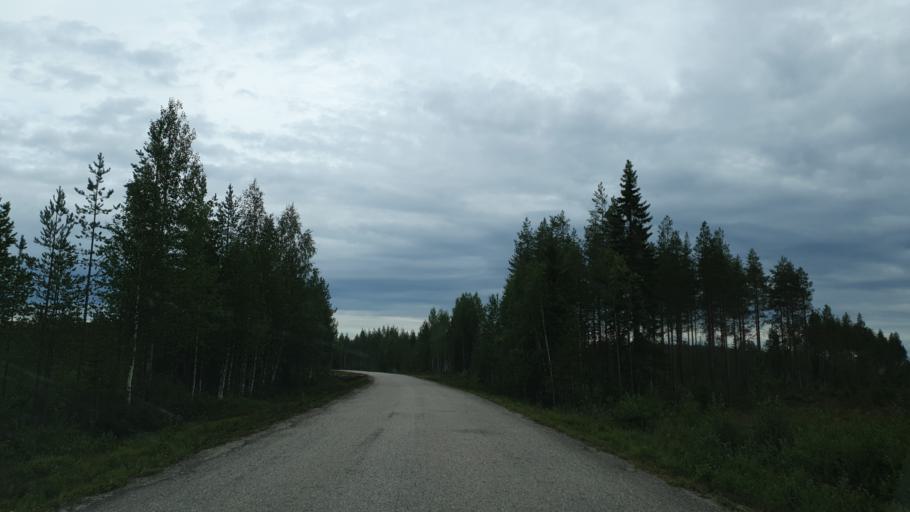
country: FI
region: Kainuu
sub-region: Kehys-Kainuu
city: Kuhmo
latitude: 64.3503
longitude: 29.1366
